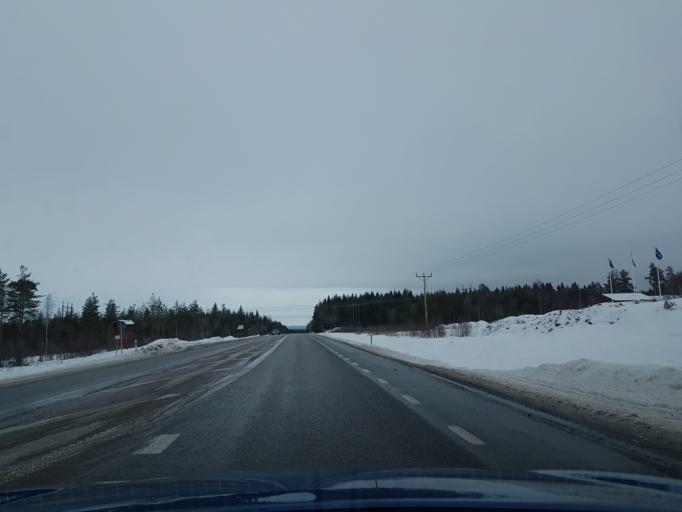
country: SE
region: Dalarna
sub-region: Mora Kommun
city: Mora
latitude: 61.0208
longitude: 14.5887
